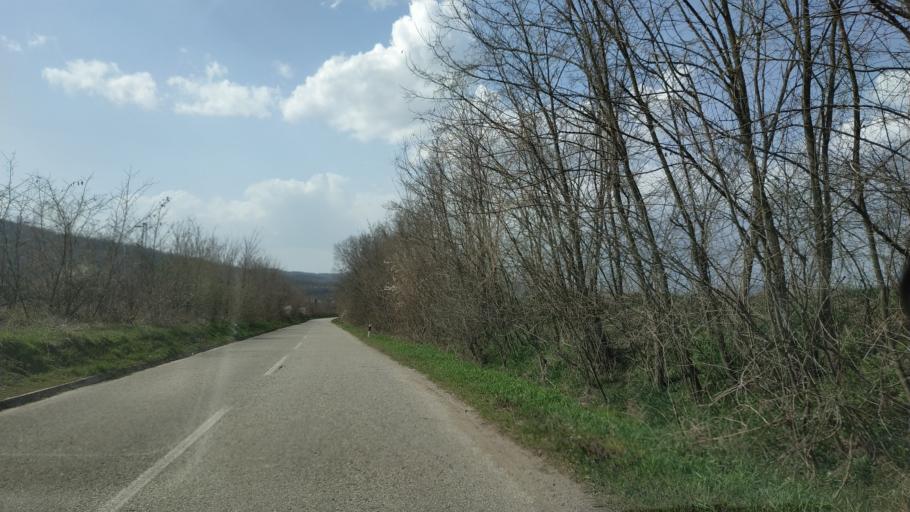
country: RS
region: Central Serbia
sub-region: Nisavski Okrug
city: Razanj
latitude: 43.5733
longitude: 21.5816
